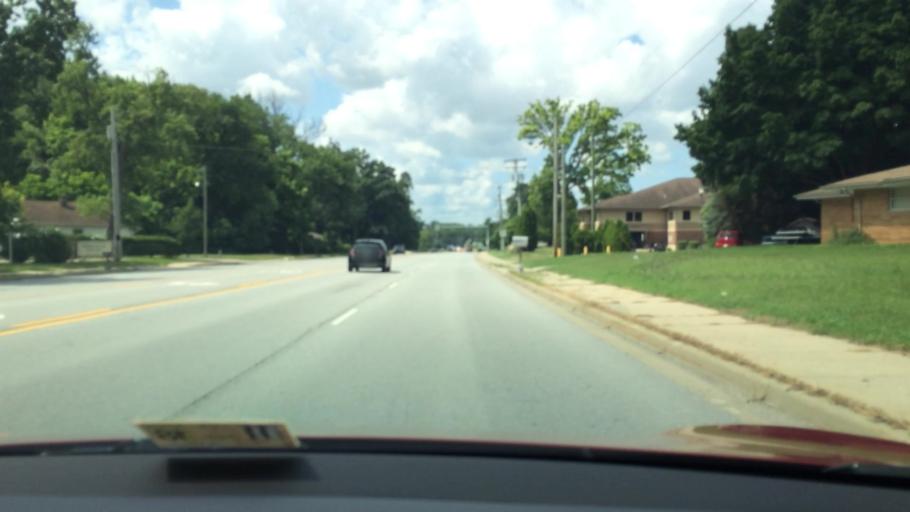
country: US
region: Indiana
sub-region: Saint Joseph County
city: Georgetown
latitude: 41.7134
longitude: -86.1997
